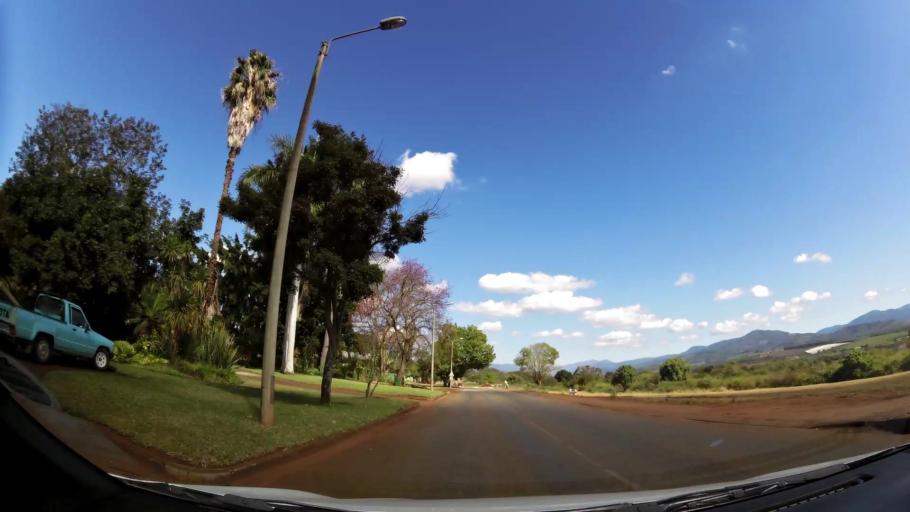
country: ZA
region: Limpopo
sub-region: Mopani District Municipality
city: Tzaneen
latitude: -23.8157
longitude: 30.1464
